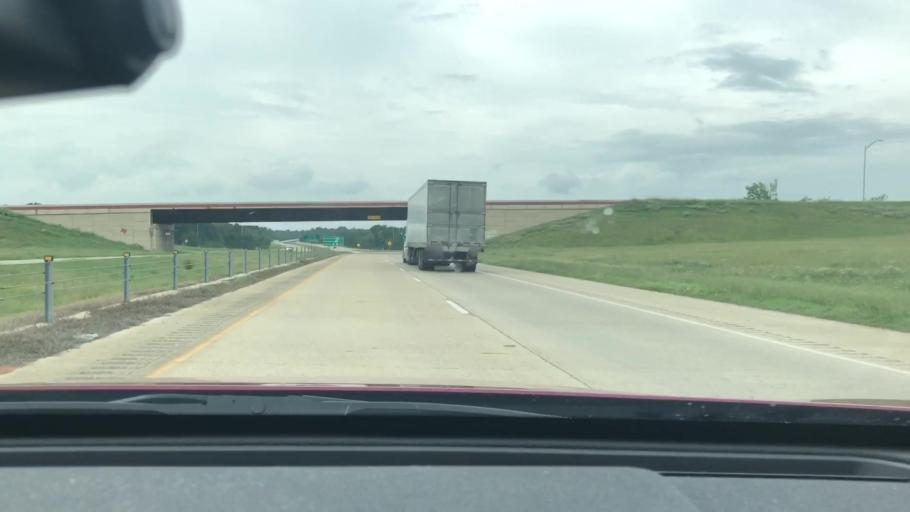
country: US
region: Texas
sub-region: Bowie County
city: Texarkana
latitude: 33.3858
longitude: -94.0417
